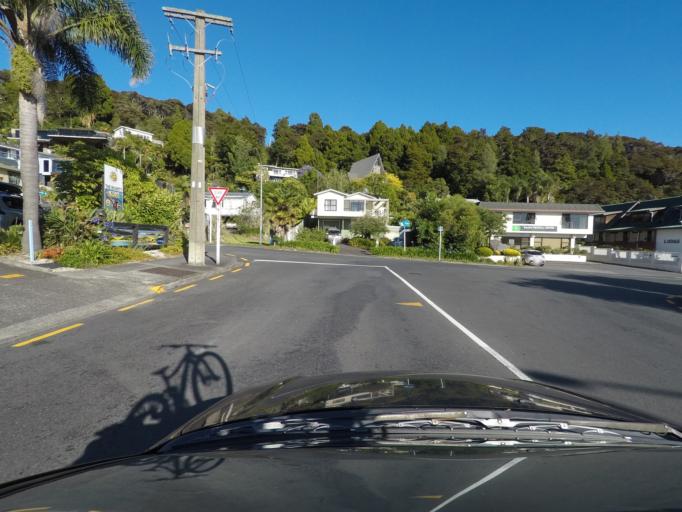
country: NZ
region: Northland
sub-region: Far North District
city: Paihia
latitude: -35.2808
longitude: 174.0893
